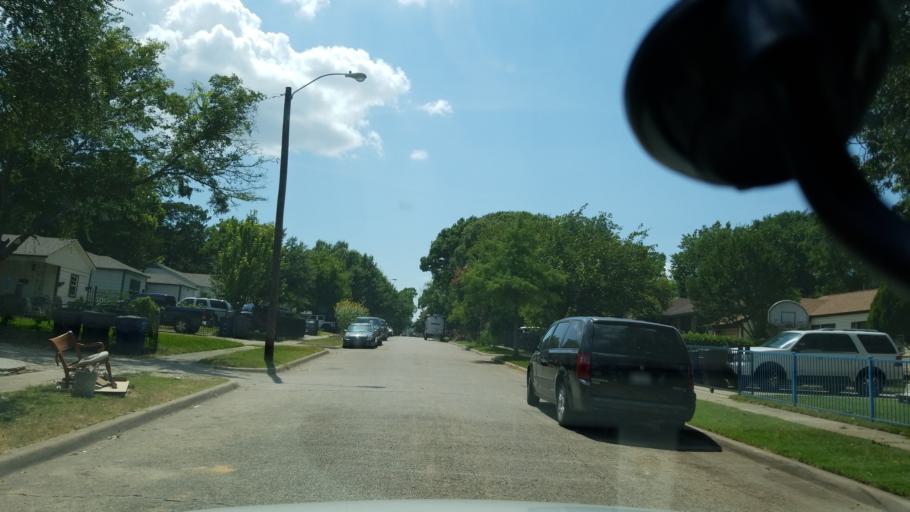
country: US
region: Texas
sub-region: Dallas County
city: Cockrell Hill
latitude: 32.7256
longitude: -96.8789
